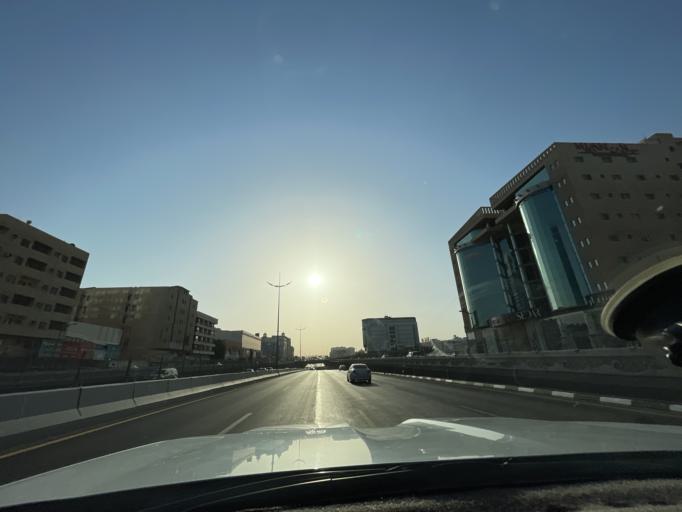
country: SA
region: Eastern Province
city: Khobar
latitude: 26.2852
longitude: 50.1933
